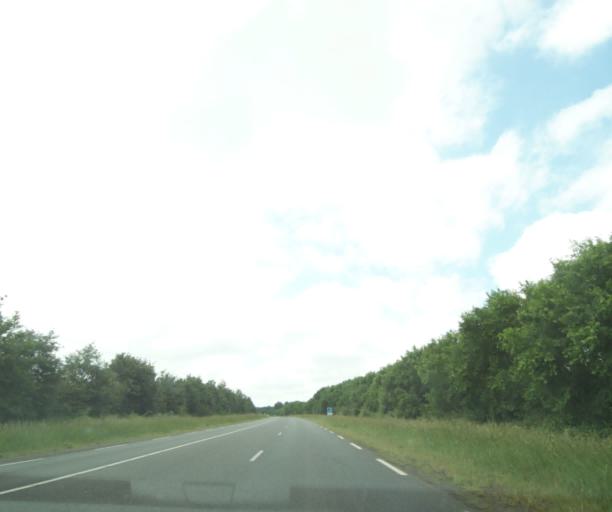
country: FR
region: Poitou-Charentes
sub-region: Departement des Deux-Sevres
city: Airvault
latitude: 46.8161
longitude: -0.2076
